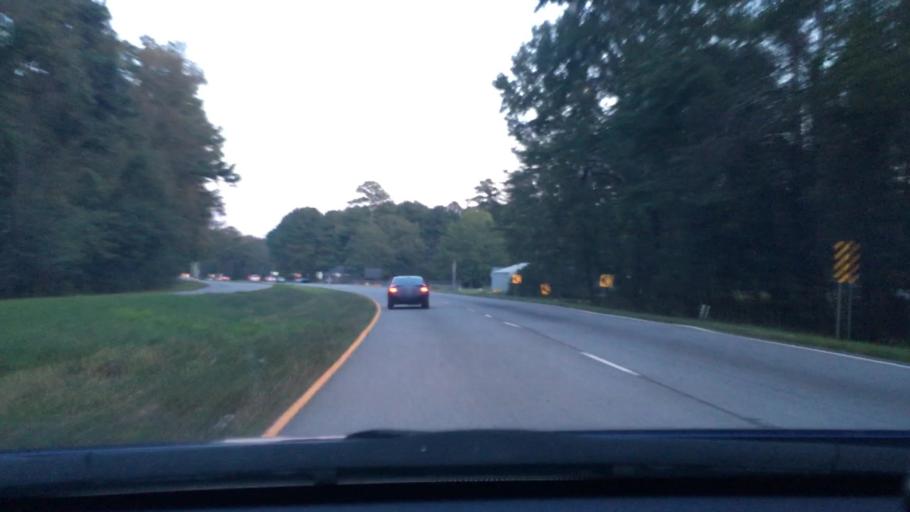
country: US
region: South Carolina
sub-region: Sumter County
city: Stateburg
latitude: 33.9432
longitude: -80.6508
